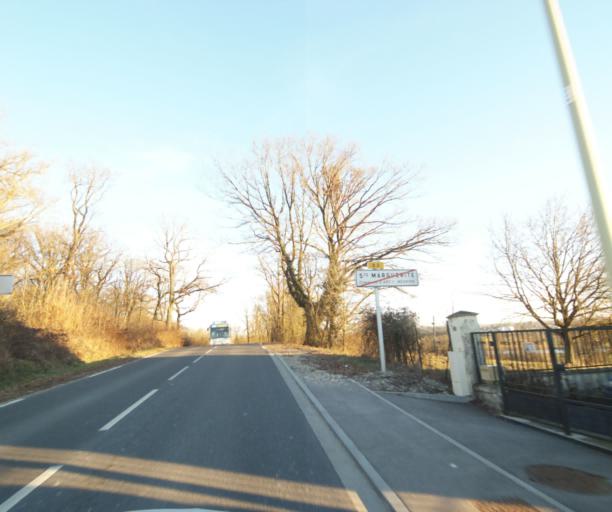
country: FR
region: Lorraine
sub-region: Departement de Meurthe-et-Moselle
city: Laneuveville-devant-Nancy
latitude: 48.6715
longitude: 6.2278
